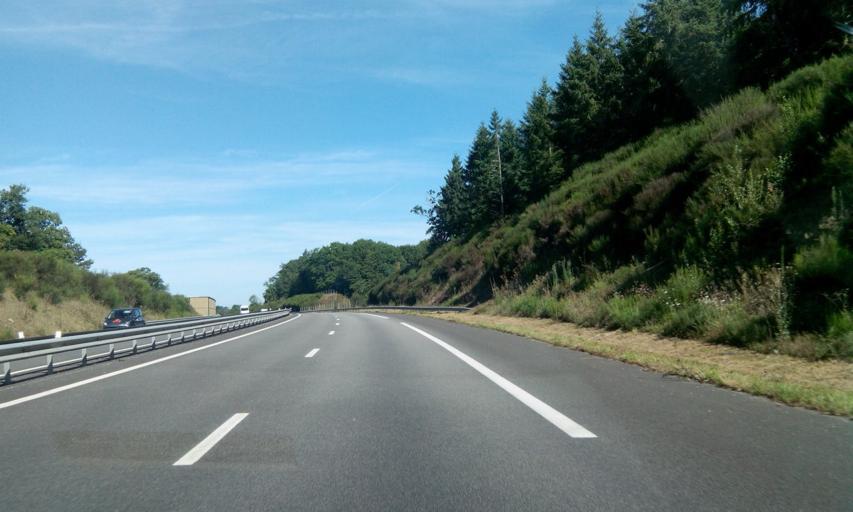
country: FR
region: Limousin
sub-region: Departement de la Haute-Vienne
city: Verneuil-sur-Vienne
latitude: 45.8725
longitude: 1.1166
